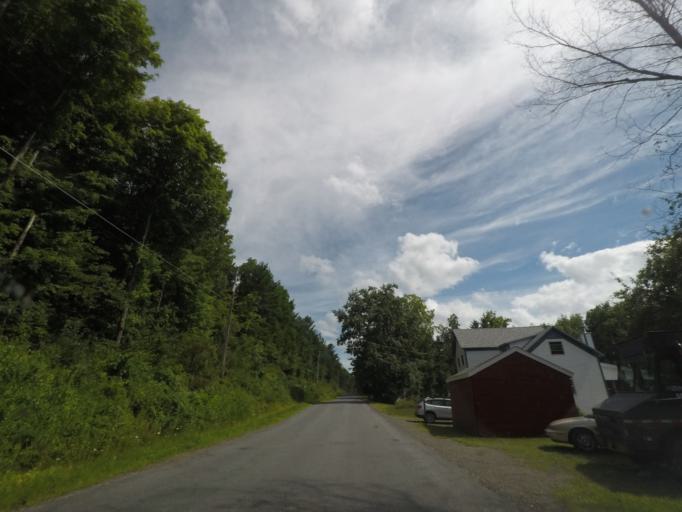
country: US
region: New York
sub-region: Rensselaer County
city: Poestenkill
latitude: 42.6695
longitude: -73.5491
